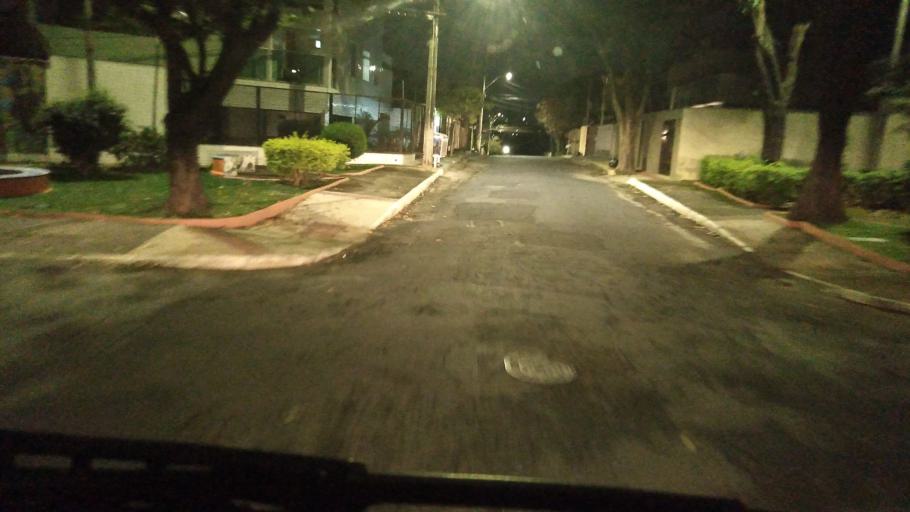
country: BR
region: Minas Gerais
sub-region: Belo Horizonte
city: Belo Horizonte
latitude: -19.9012
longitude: -43.9166
